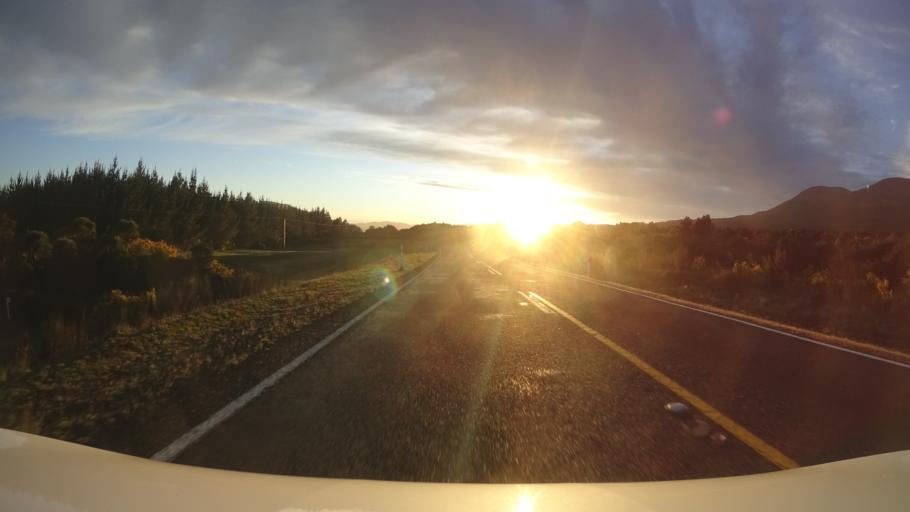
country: NZ
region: Waikato
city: Turangi
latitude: -39.0647
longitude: 175.6519
